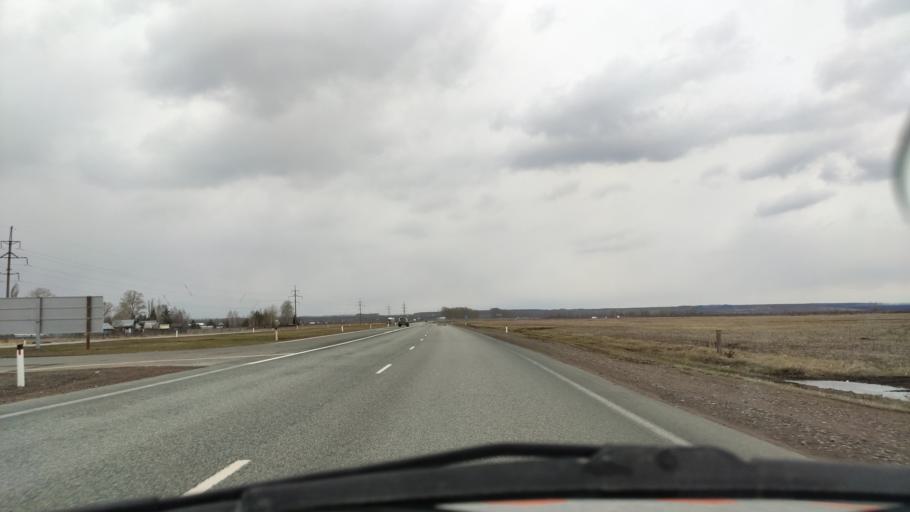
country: RU
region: Bashkortostan
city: Asanovo
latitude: 54.9983
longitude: 55.5021
